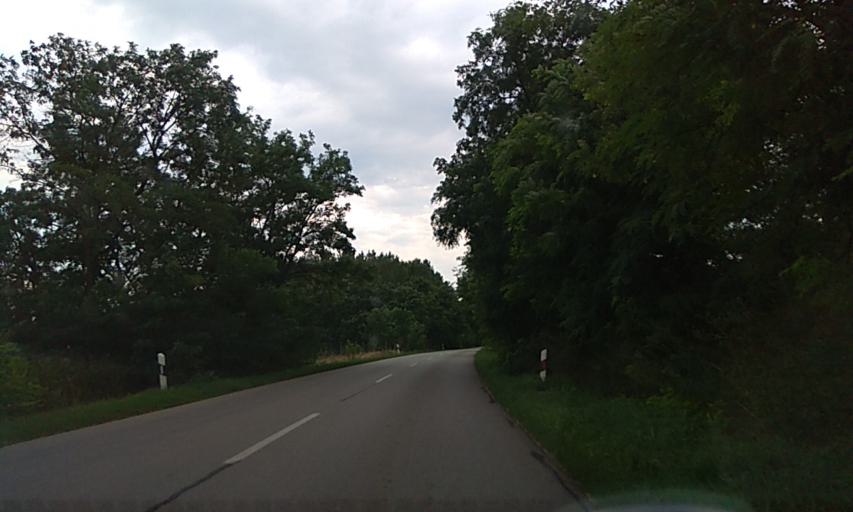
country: HU
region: Szabolcs-Szatmar-Bereg
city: Buj
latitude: 48.0806
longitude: 21.6408
